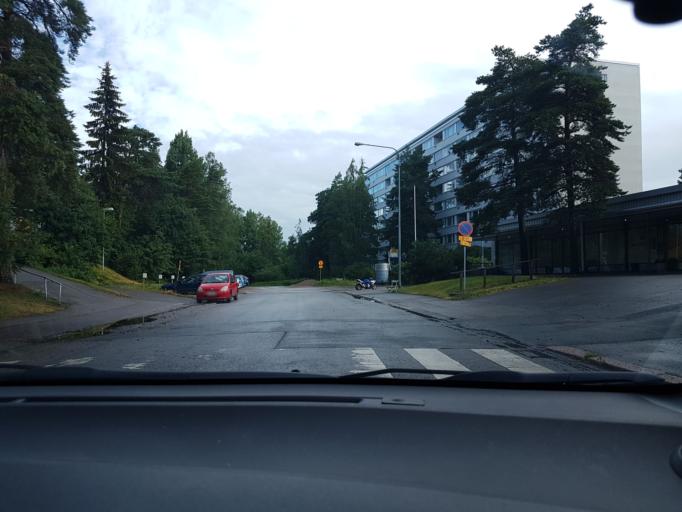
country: FI
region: Uusimaa
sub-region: Helsinki
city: Vantaa
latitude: 60.2372
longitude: 25.0094
